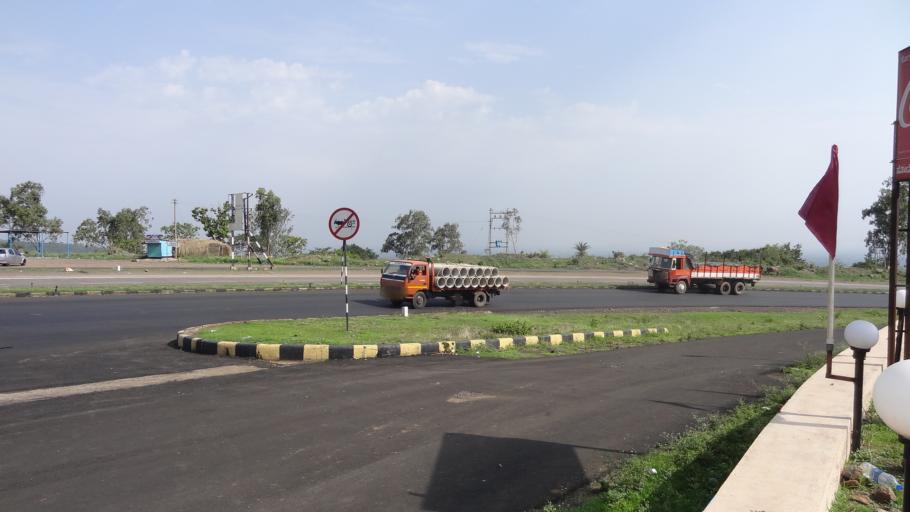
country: IN
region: Maharashtra
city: Nipani
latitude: 16.3485
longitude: 74.3945
